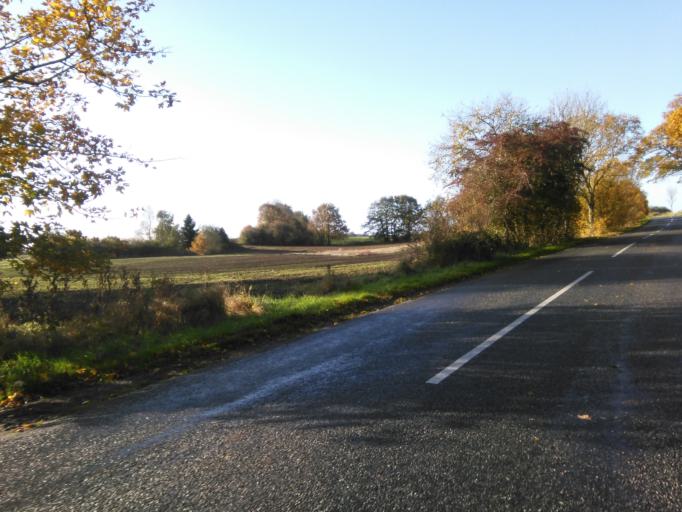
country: DK
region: Central Jutland
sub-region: Arhus Kommune
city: Malling
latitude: 56.0342
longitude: 10.1732
